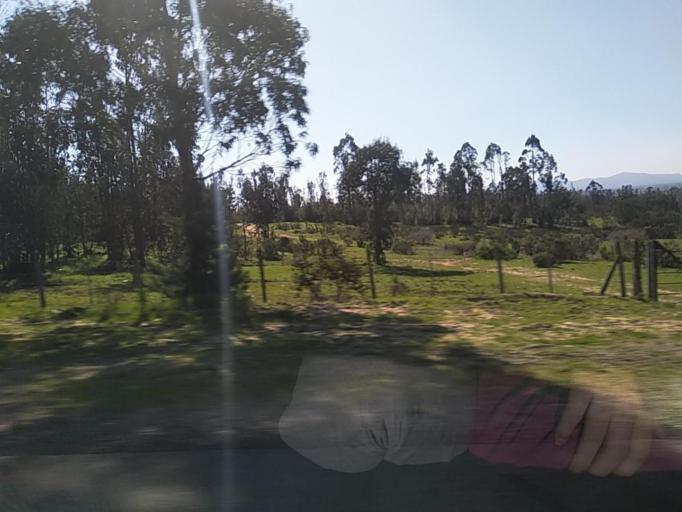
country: CL
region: Valparaiso
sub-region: San Antonio Province
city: El Tabo
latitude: -33.4083
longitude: -71.5527
